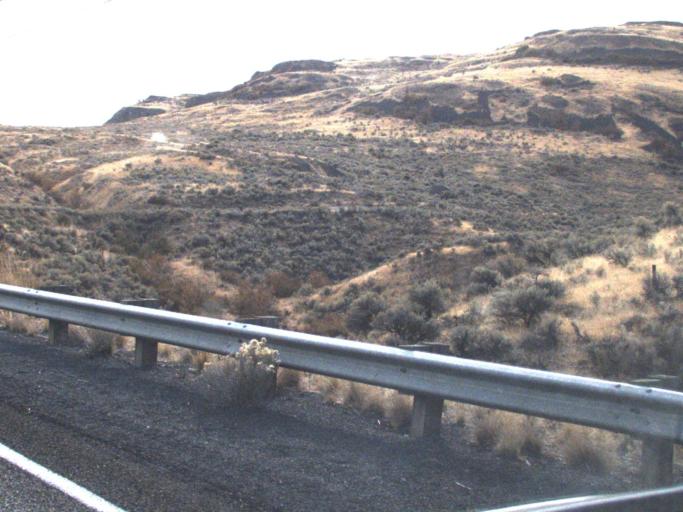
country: US
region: Washington
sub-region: Okanogan County
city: Coulee Dam
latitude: 47.9259
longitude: -118.9629
